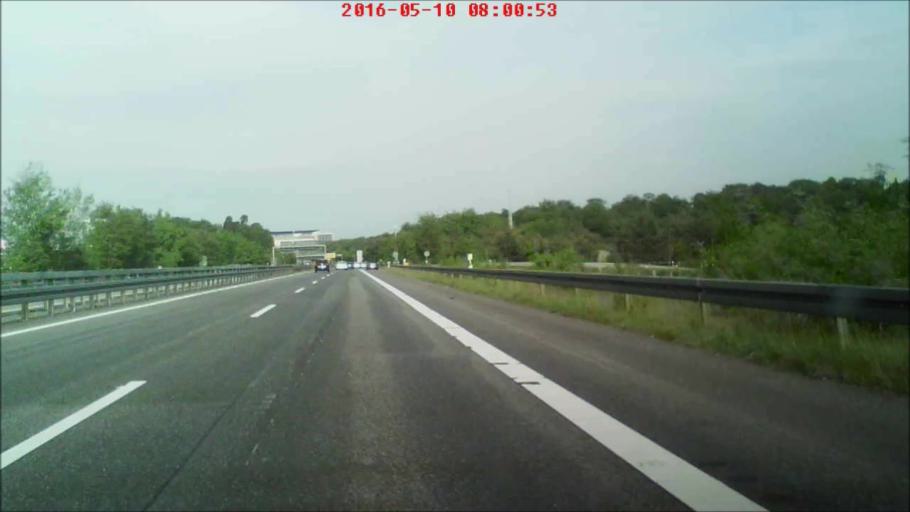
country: DE
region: Hesse
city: Niederrad
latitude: 50.0566
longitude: 8.6120
